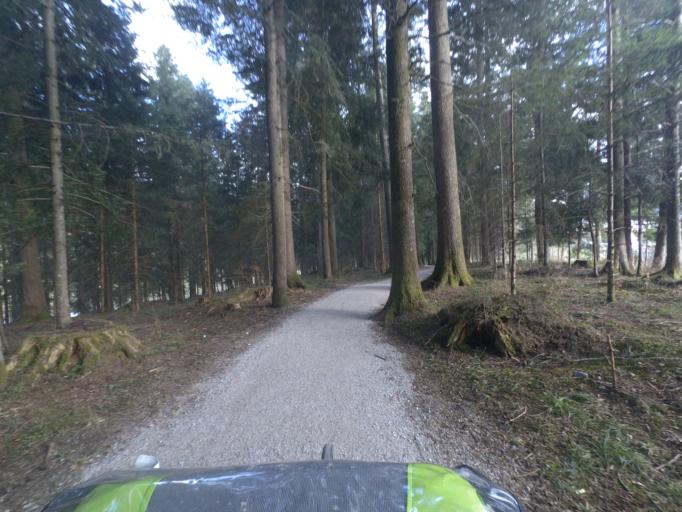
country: AT
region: Salzburg
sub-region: Politischer Bezirk Hallein
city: Abtenau
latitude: 47.5712
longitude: 13.3505
